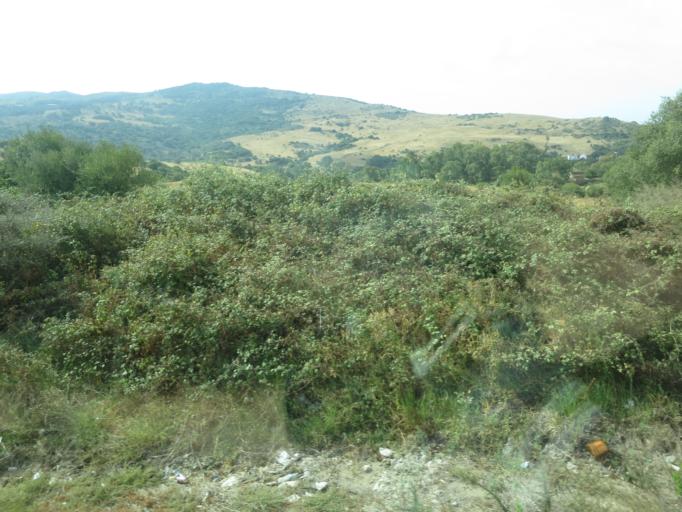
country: ES
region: Andalusia
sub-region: Provincia de Cadiz
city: Algeciras
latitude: 36.0874
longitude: -5.4900
